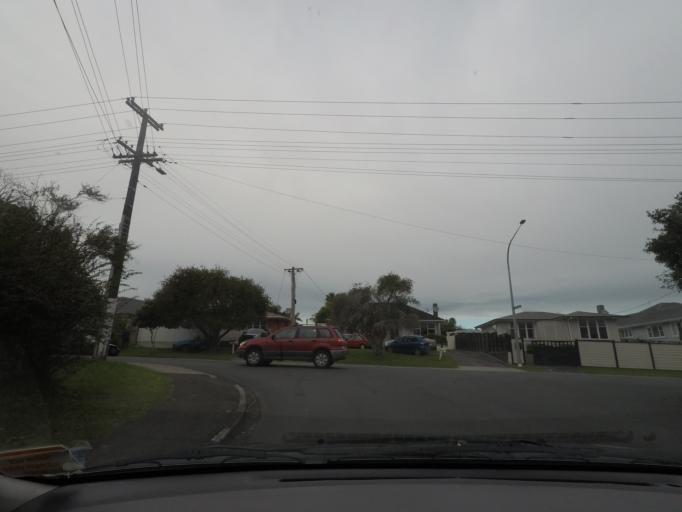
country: NZ
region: Auckland
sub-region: Auckland
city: Rosebank
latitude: -36.8629
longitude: 174.6445
